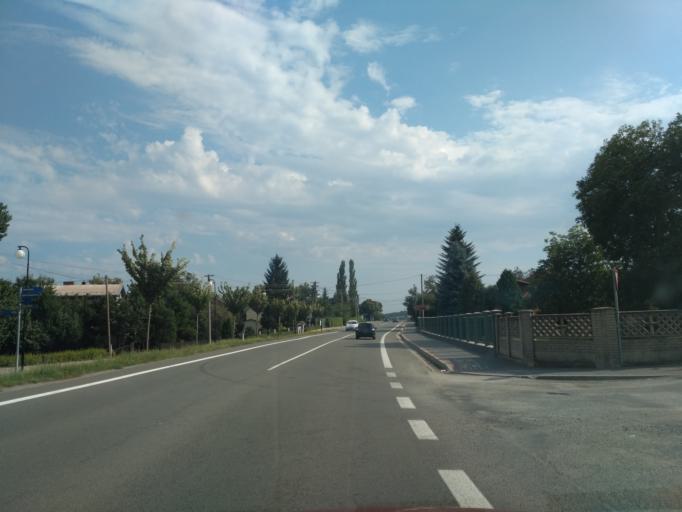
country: SK
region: Kosicky
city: Kosice
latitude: 48.7972
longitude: 21.3054
